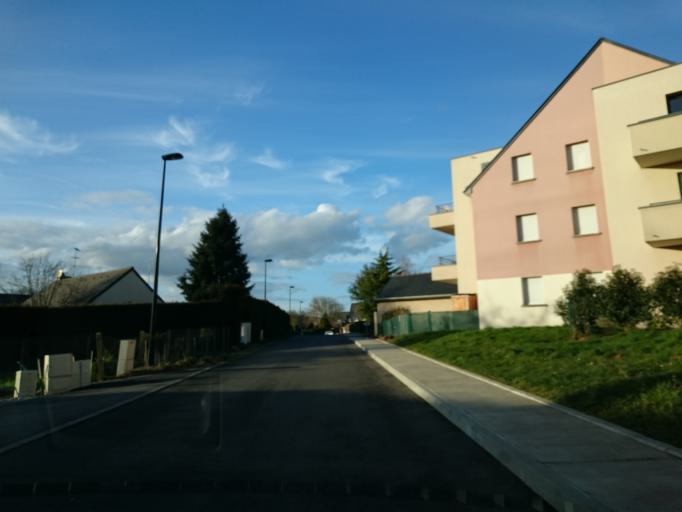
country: FR
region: Brittany
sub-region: Departement d'Ille-et-Vilaine
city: Crevin
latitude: 47.9351
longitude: -1.6632
